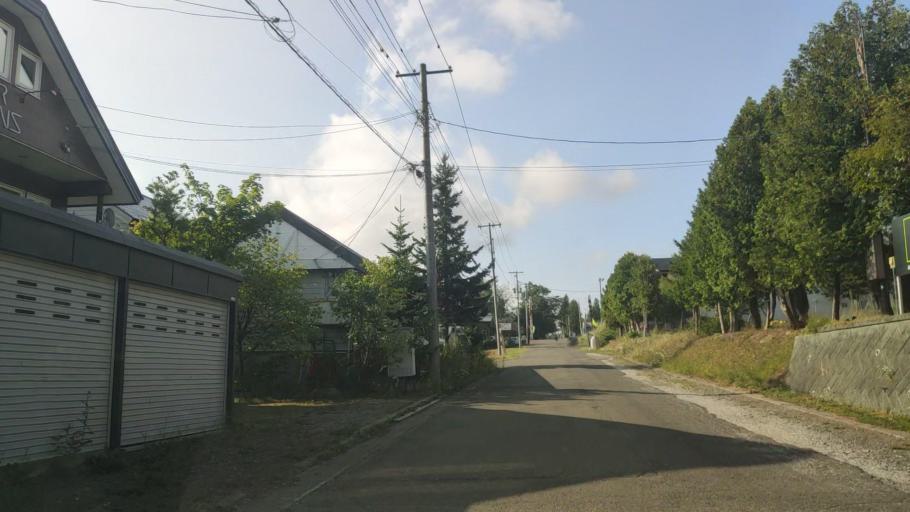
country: JP
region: Hokkaido
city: Shimo-furano
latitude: 43.3448
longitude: 142.3629
